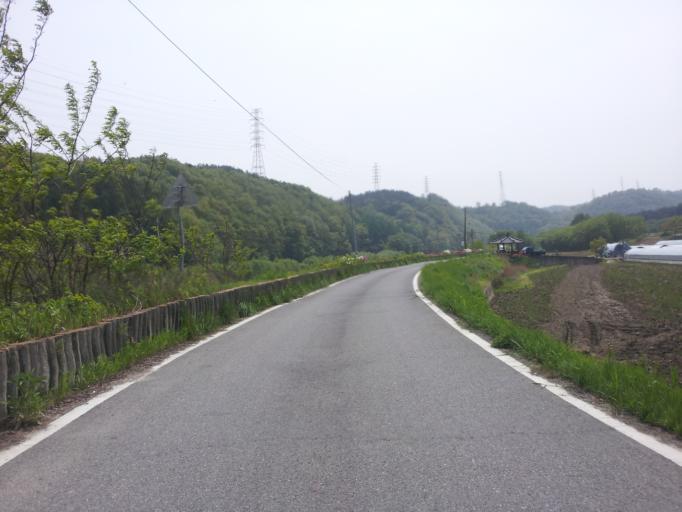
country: KR
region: Daejeon
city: Daejeon
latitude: 36.2639
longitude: 127.2963
